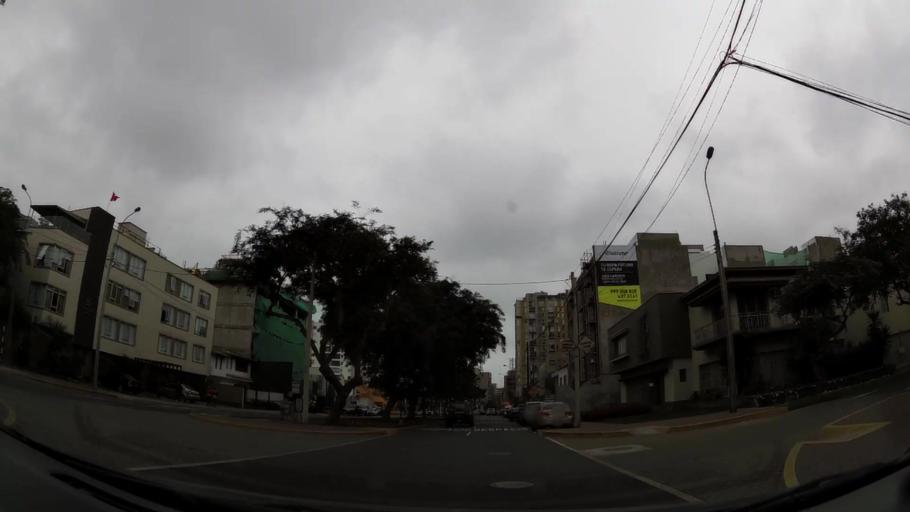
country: PE
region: Lima
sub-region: Lima
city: Surco
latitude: -12.1215
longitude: -77.0230
